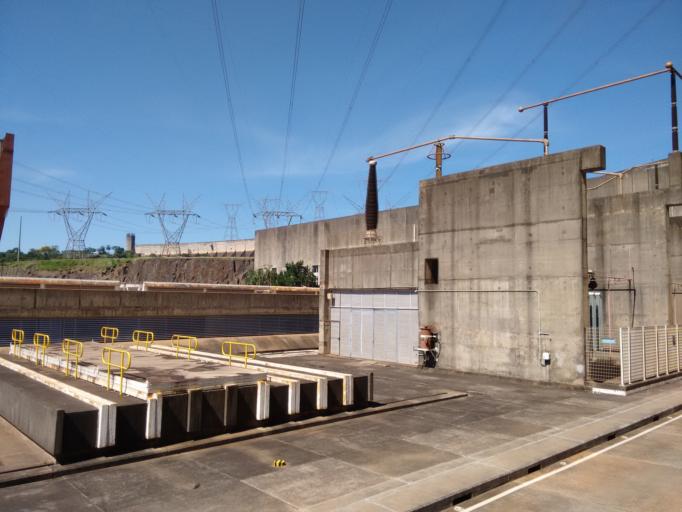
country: PY
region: Alto Parana
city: Ciudad del Este
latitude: -25.4073
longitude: -54.5925
